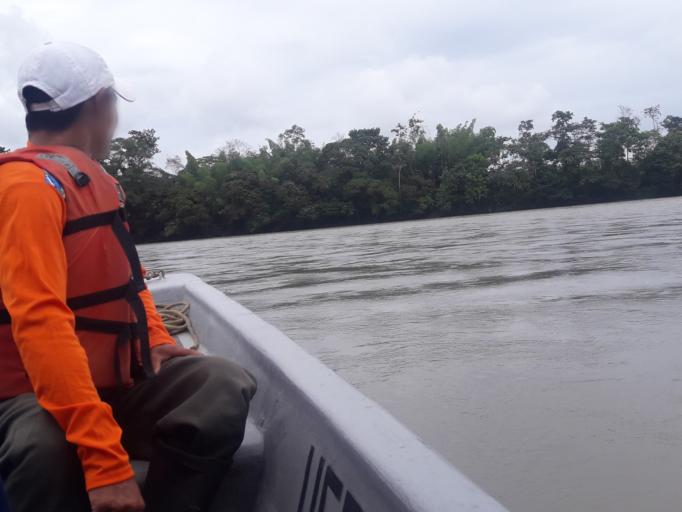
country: EC
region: Orellana
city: Boca Suno
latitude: -0.8793
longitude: -77.2851
